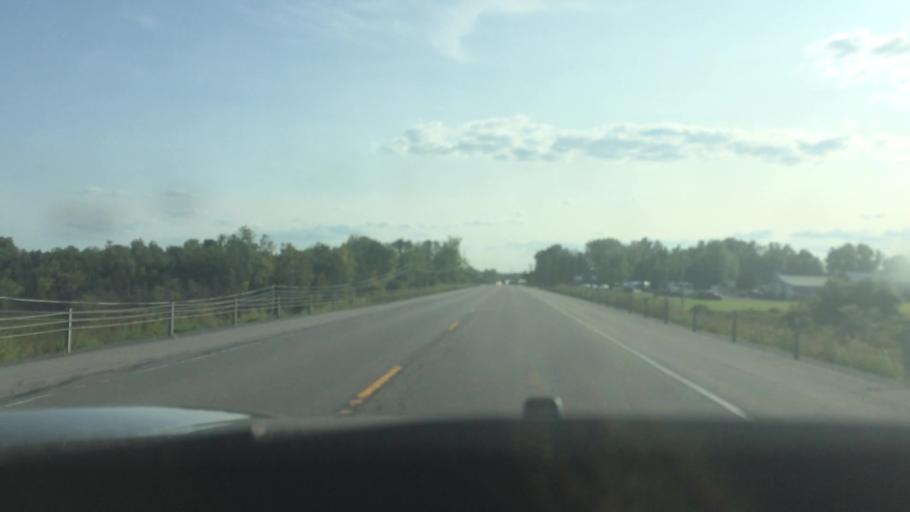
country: US
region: New York
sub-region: St. Lawrence County
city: Potsdam
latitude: 44.6565
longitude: -75.0391
